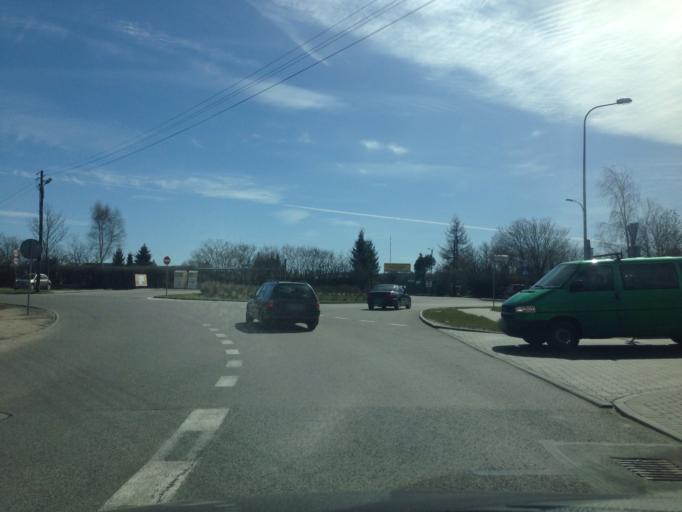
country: PL
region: Pomeranian Voivodeship
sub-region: Powiat kartuski
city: Chwaszczyno
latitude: 54.4825
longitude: 18.4371
